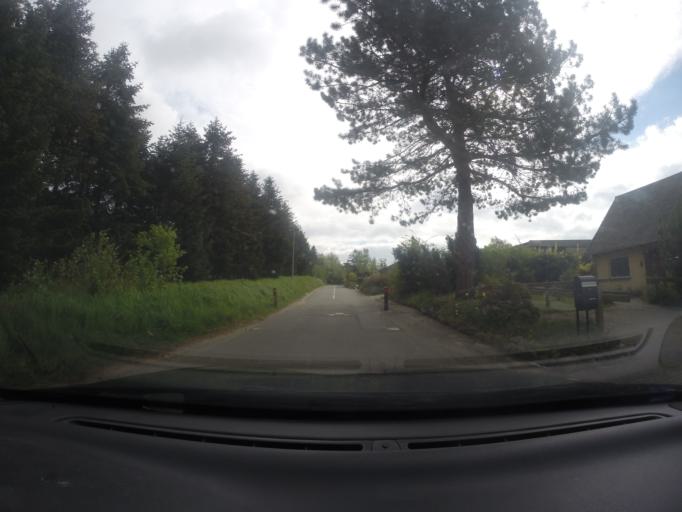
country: DK
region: Capital Region
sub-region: Hoje-Taastrup Kommune
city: Taastrup
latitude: 55.6849
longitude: 12.2990
